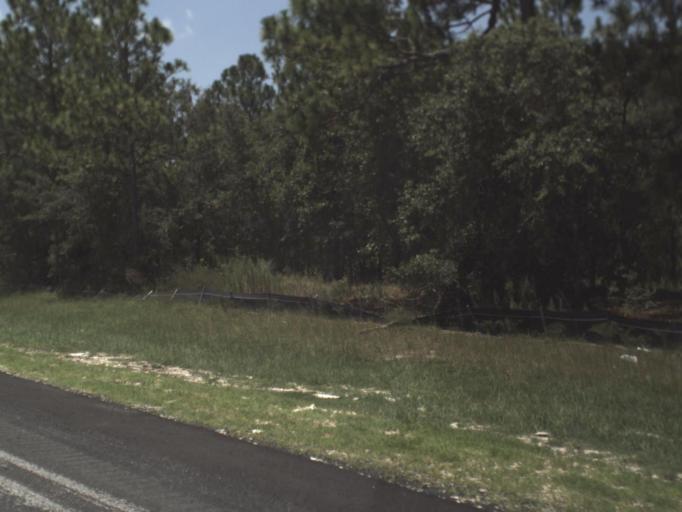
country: US
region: Florida
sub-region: Citrus County
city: Sugarmill Woods
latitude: 28.6768
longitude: -82.5525
